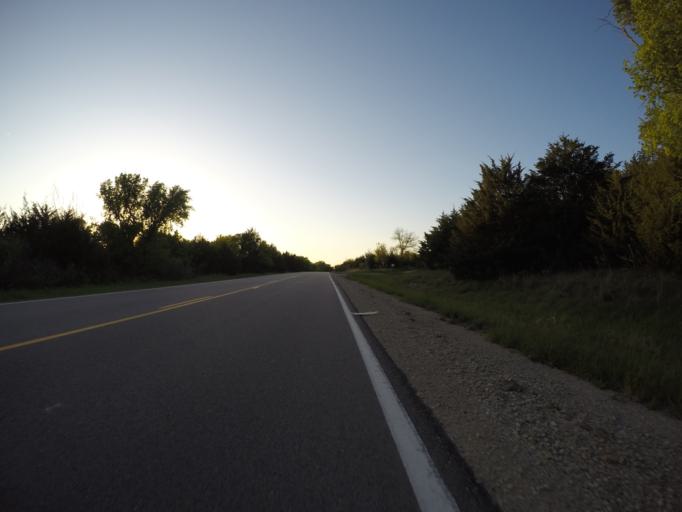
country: US
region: Kansas
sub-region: Riley County
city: Fort Riley North
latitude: 39.2438
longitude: -96.7657
